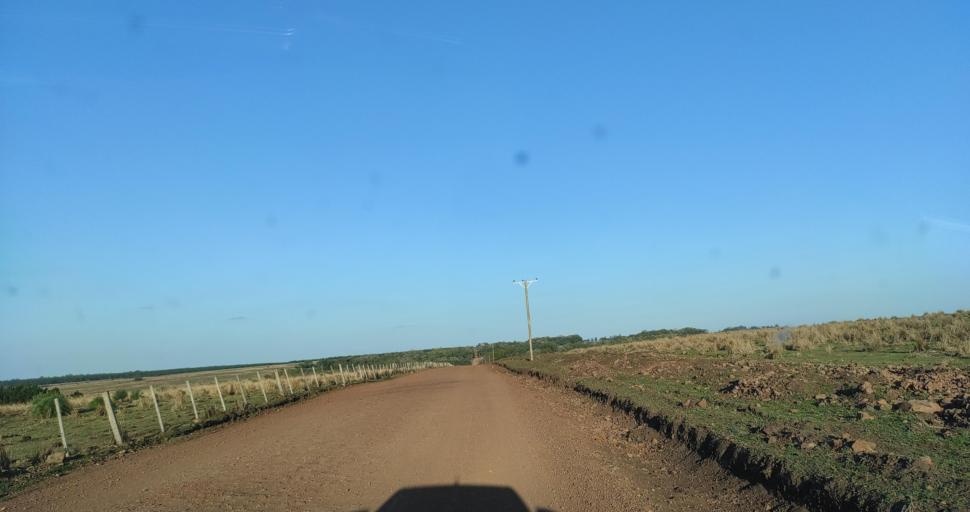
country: PY
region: Itapua
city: Carmen del Parana
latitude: -27.4149
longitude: -56.1356
